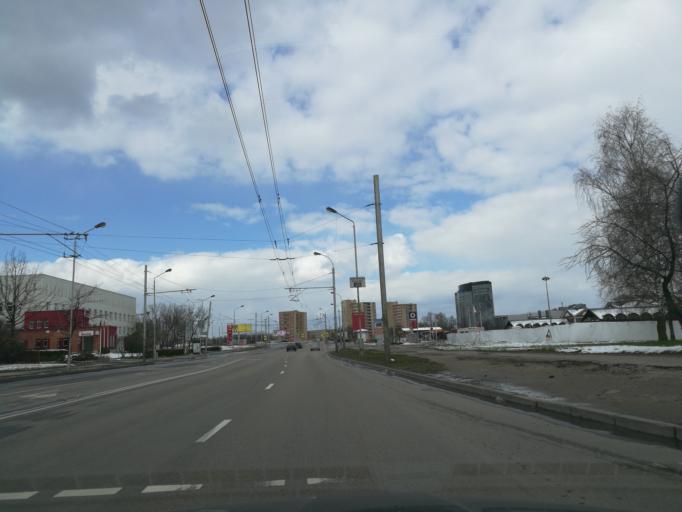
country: LT
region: Kauno apskritis
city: Dainava (Kaunas)
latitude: 54.9138
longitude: 23.9856
